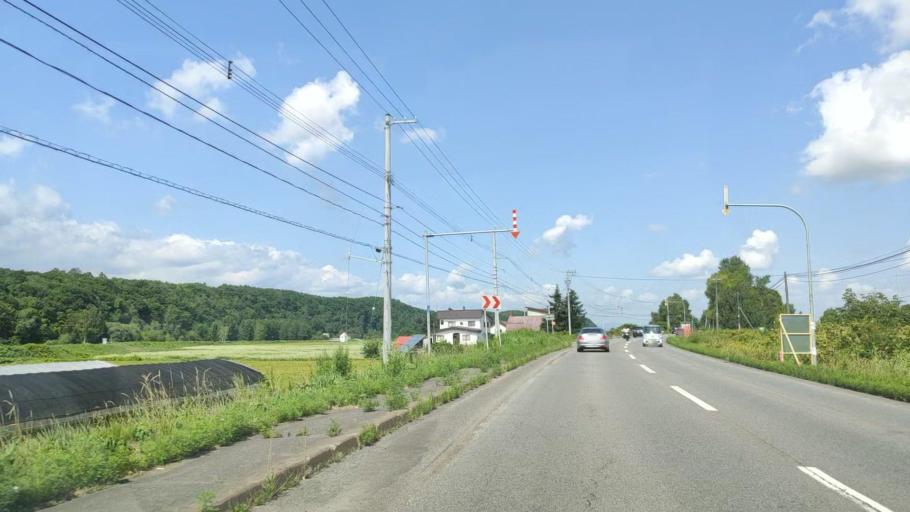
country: JP
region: Hokkaido
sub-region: Asahikawa-shi
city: Asahikawa
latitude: 43.6318
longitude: 142.4592
